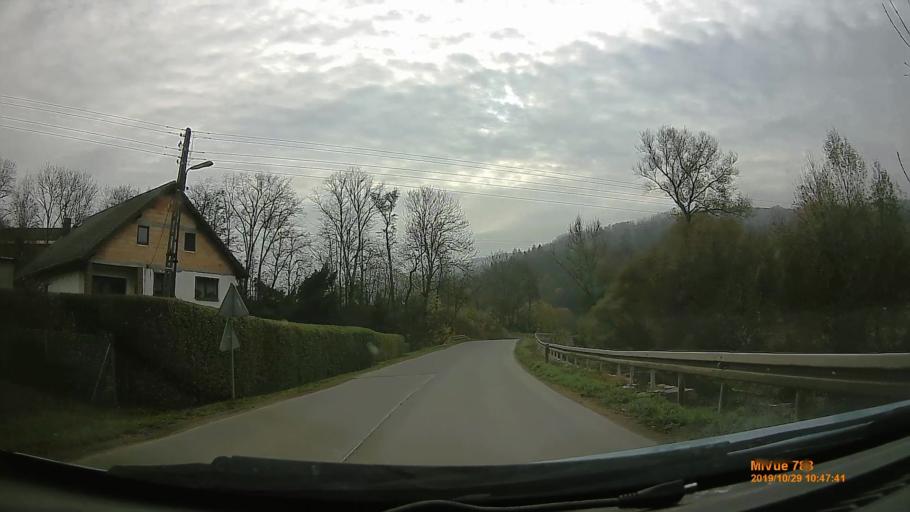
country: PL
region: Lower Silesian Voivodeship
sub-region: Powiat klodzki
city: Radkow
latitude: 50.5537
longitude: 16.4350
